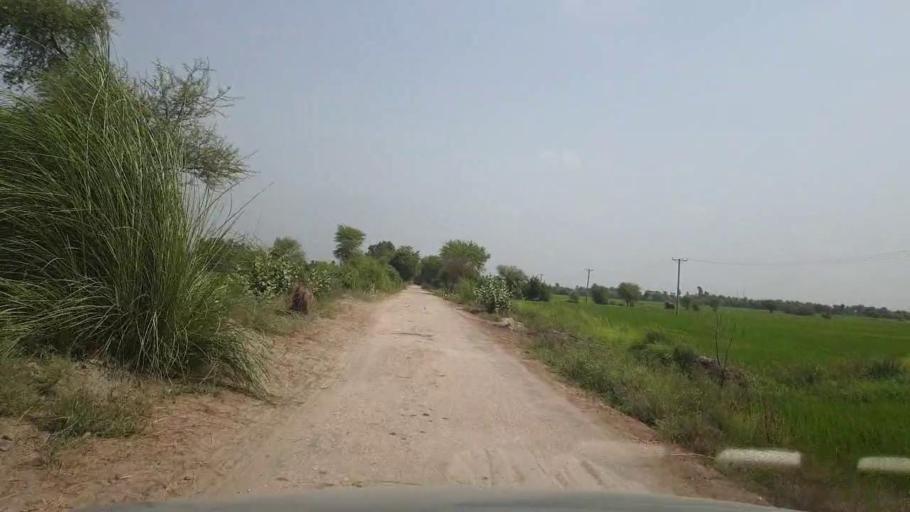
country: PK
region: Sindh
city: Garhi Yasin
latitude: 27.9468
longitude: 68.3757
